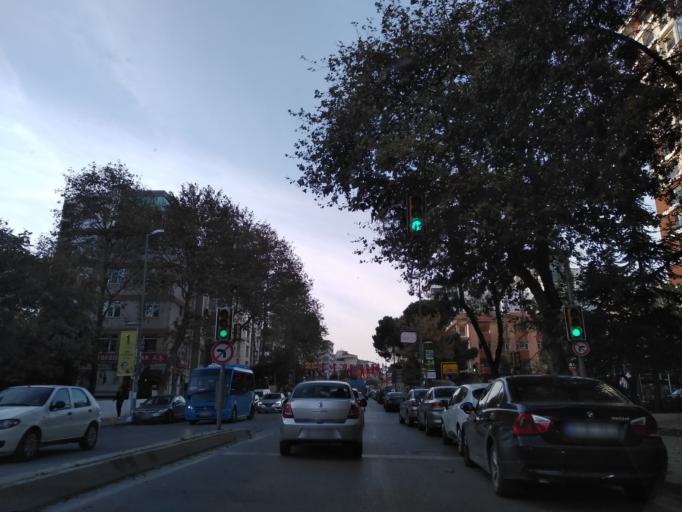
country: TR
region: Istanbul
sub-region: Atasehir
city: Atasehir
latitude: 40.9643
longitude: 29.0888
